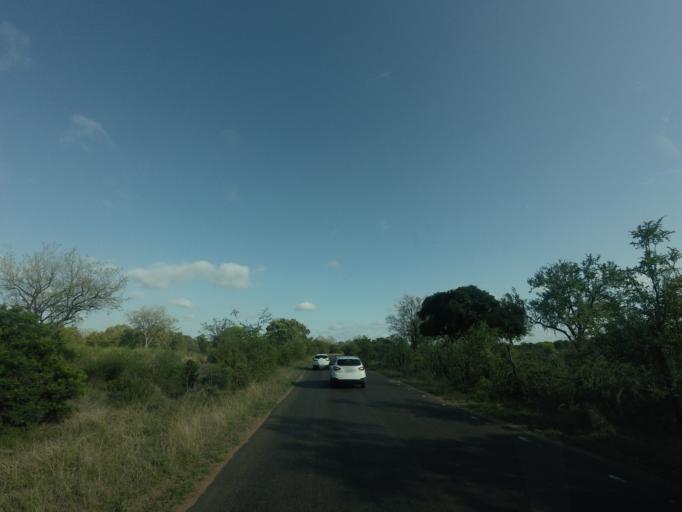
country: ZA
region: Mpumalanga
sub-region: Ehlanzeni District
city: Komatipoort
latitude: -25.2756
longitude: 31.8488
